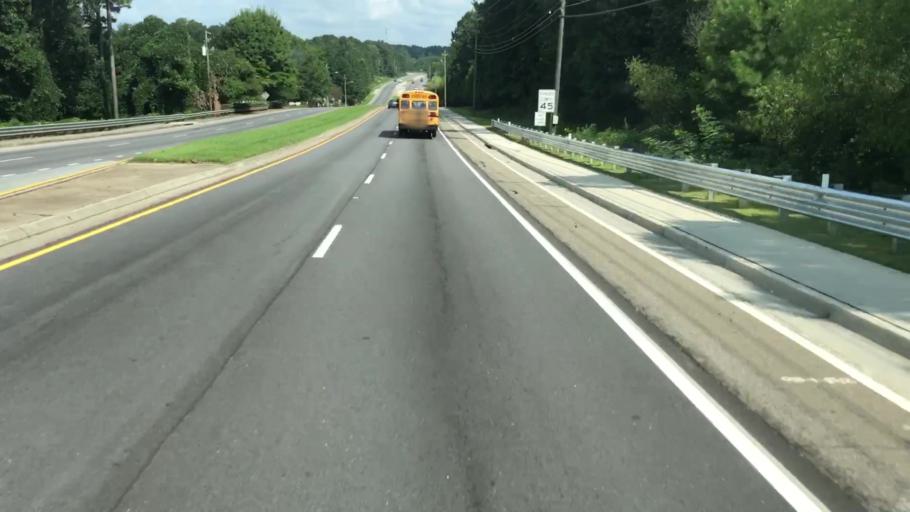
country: US
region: Georgia
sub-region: Gwinnett County
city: Lawrenceville
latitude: 33.9289
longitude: -84.0256
